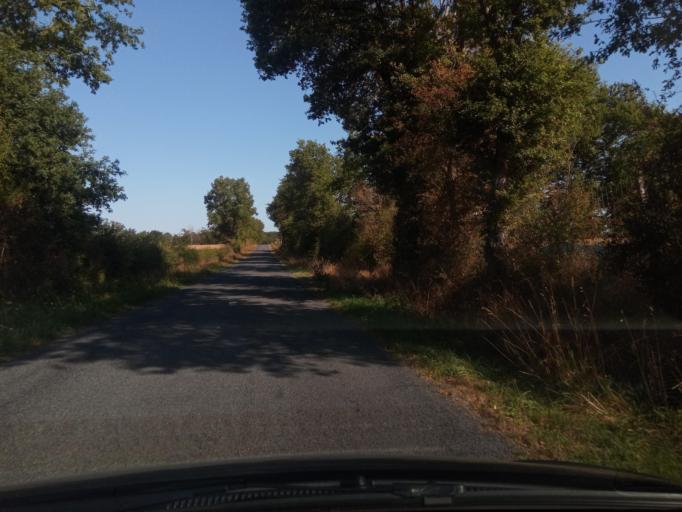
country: FR
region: Poitou-Charentes
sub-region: Departement de la Vienne
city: Saulge
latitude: 46.3385
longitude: 0.8743
